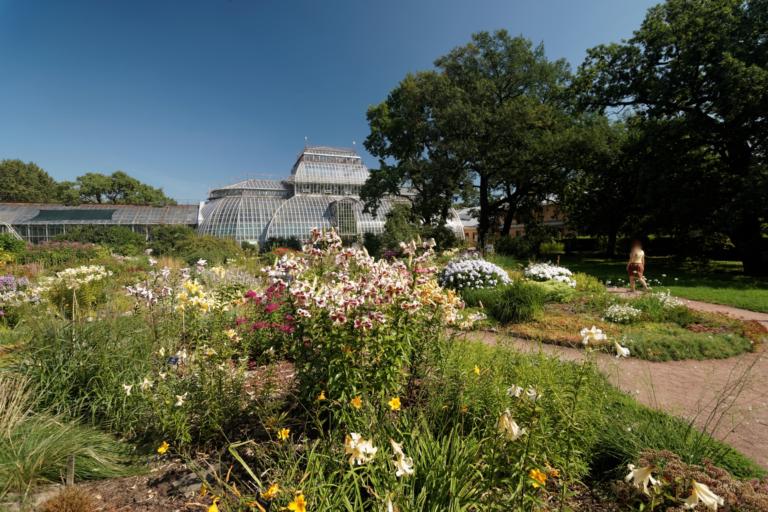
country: RU
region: St.-Petersburg
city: Petrogradka
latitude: 59.9711
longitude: 30.3235
